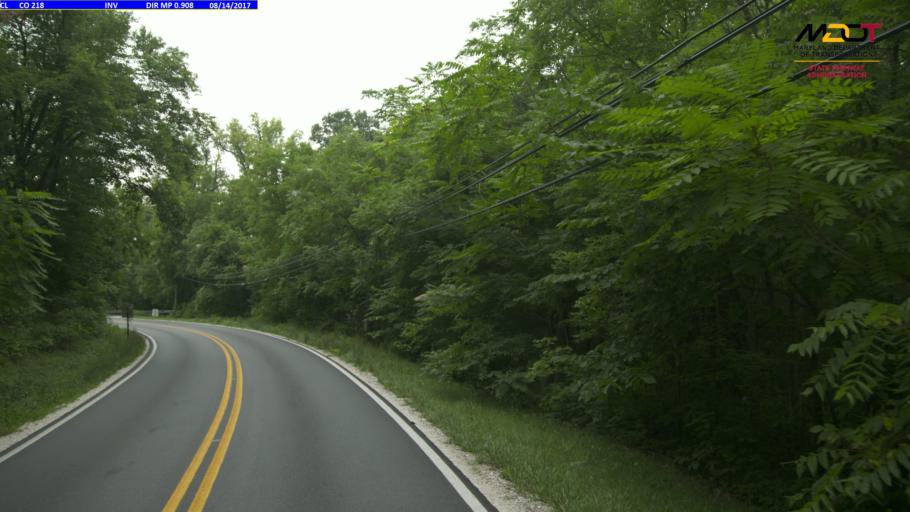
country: US
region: Maryland
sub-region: Carroll County
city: Taneytown
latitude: 39.5826
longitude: -77.1798
